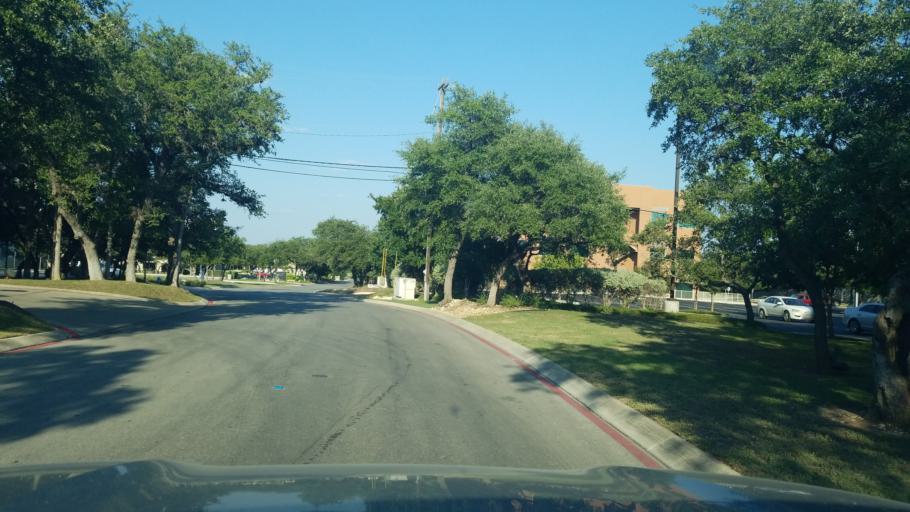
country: US
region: Texas
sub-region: Bexar County
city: Shavano Park
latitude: 29.6000
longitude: -98.5531
